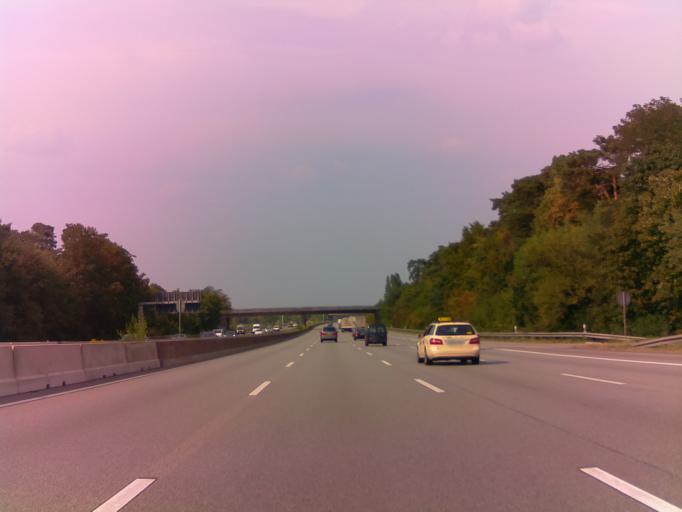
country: DE
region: Hesse
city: Weiterstadt
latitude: 49.9069
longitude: 8.6077
